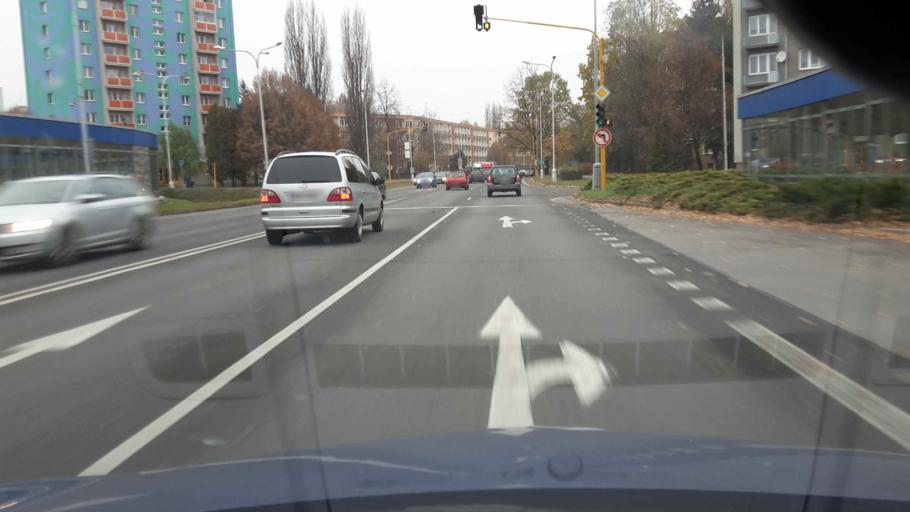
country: CZ
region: Olomoucky
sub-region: Okres Olomouc
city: Olomouc
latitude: 49.5915
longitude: 17.2355
